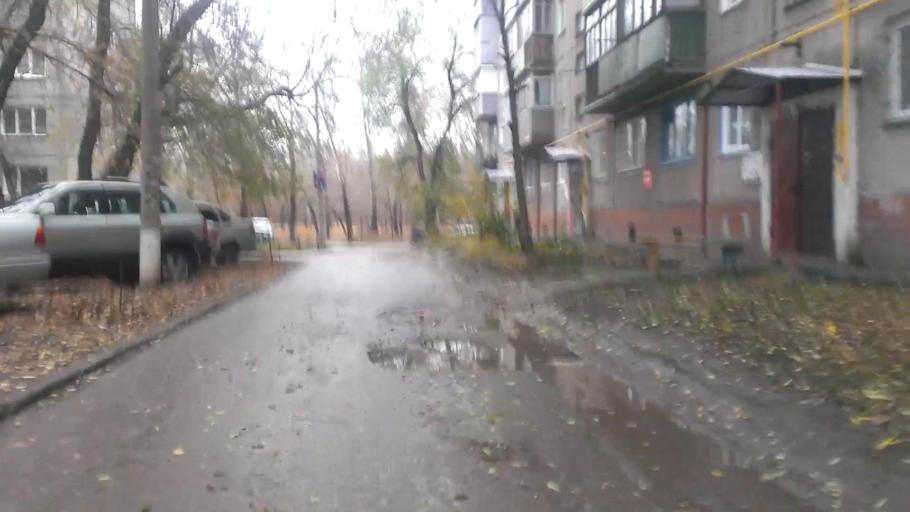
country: RU
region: Altai Krai
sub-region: Gorod Barnaulskiy
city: Barnaul
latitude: 53.3631
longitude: 83.6866
